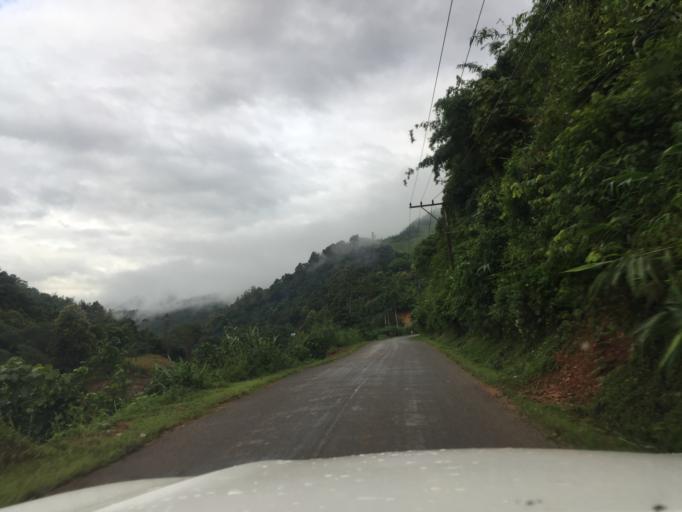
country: LA
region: Oudomxai
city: Muang La
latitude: 20.9136
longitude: 102.1920
